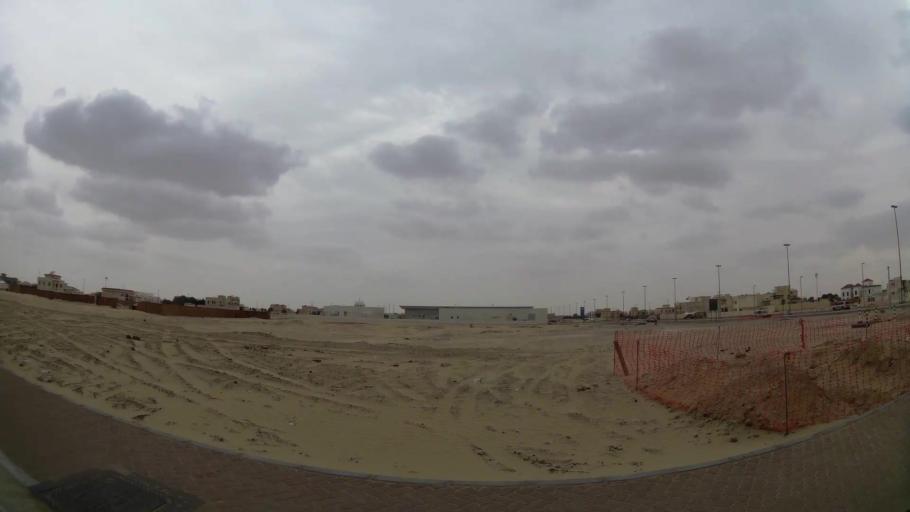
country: AE
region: Abu Dhabi
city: Abu Dhabi
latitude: 24.3691
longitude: 54.6237
